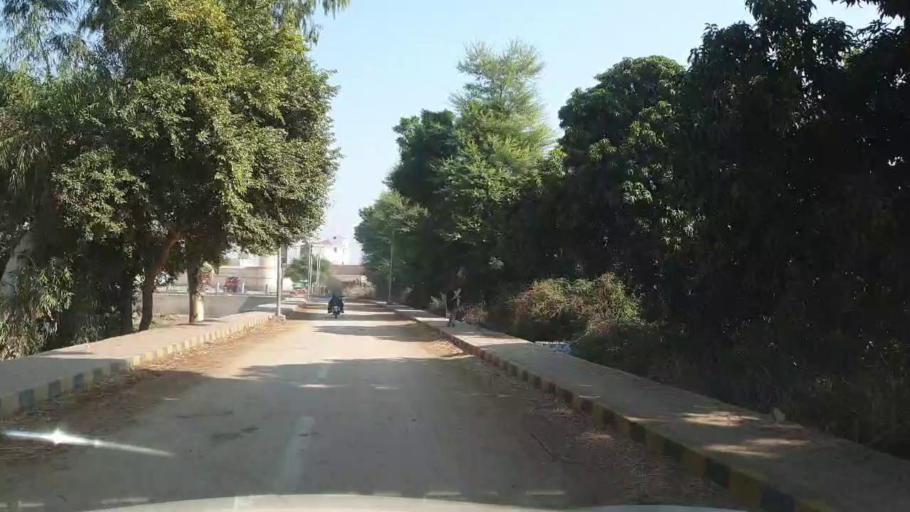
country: PK
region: Sindh
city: Bhan
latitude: 26.5405
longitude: 67.7774
